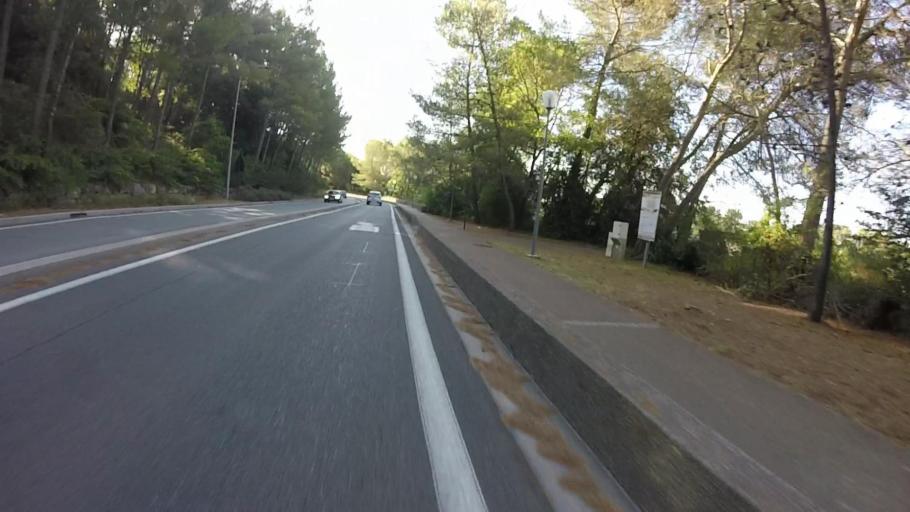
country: FR
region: Provence-Alpes-Cote d'Azur
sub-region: Departement des Alpes-Maritimes
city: Mougins
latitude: 43.6107
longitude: 7.0186
